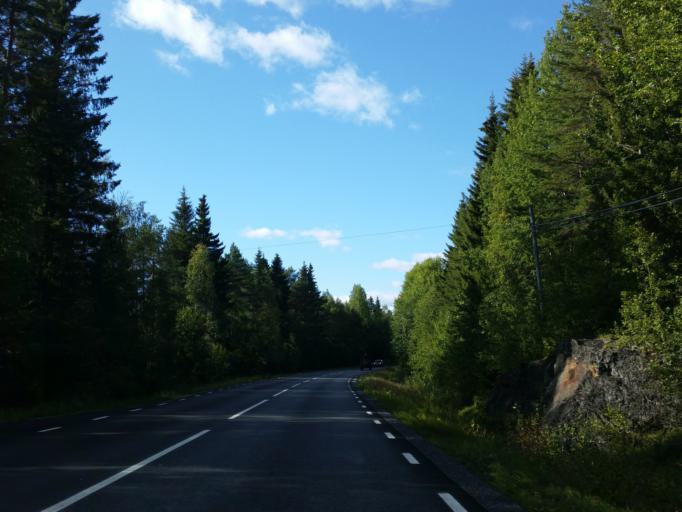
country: SE
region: Vaesterbotten
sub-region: Robertsfors Kommun
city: Robertsfors
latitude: 64.1620
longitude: 20.9366
